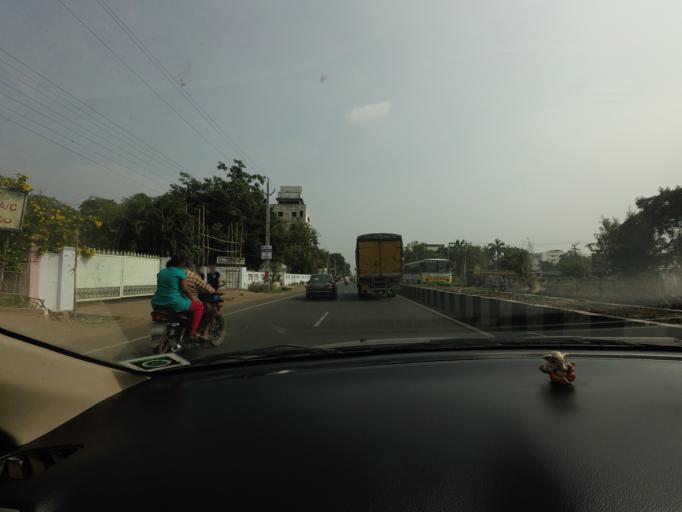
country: IN
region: Andhra Pradesh
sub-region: Krishna
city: Yanamalakuduru
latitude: 16.4861
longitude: 80.6810
